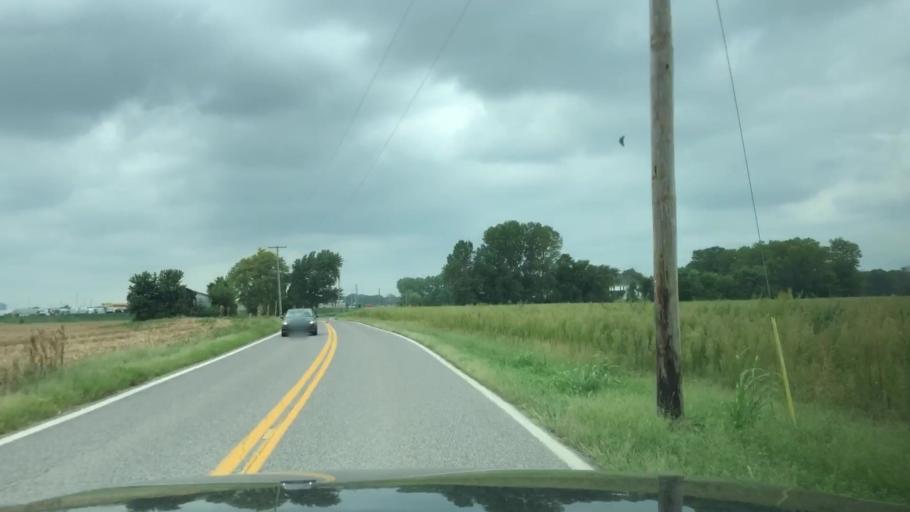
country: US
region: Missouri
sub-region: Saint Charles County
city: Saint Charles
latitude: 38.7966
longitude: -90.4425
